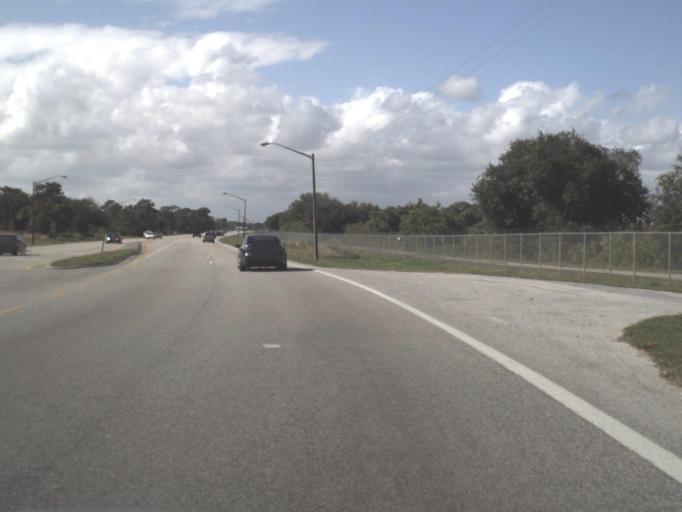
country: US
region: Florida
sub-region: Brevard County
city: West Melbourne
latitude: 28.0981
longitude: -80.6559
